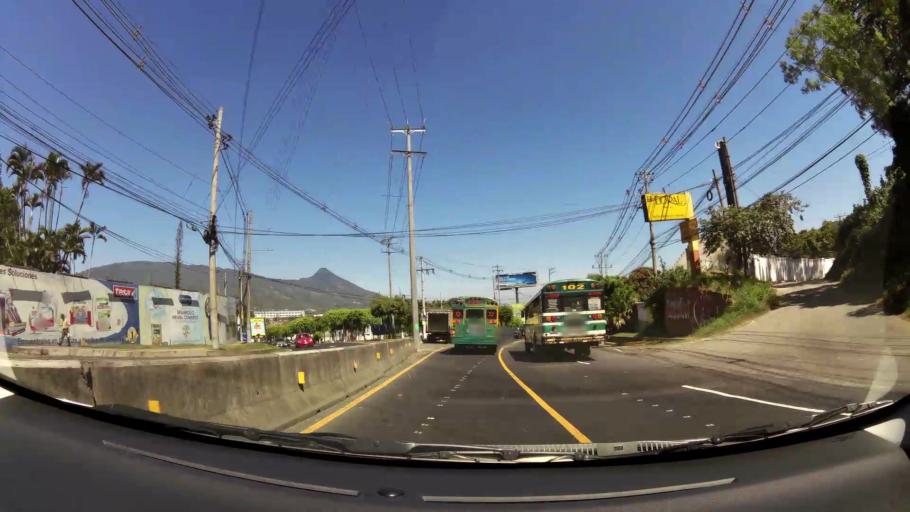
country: SV
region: La Libertad
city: Santa Tecla
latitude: 13.6622
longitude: -89.2783
